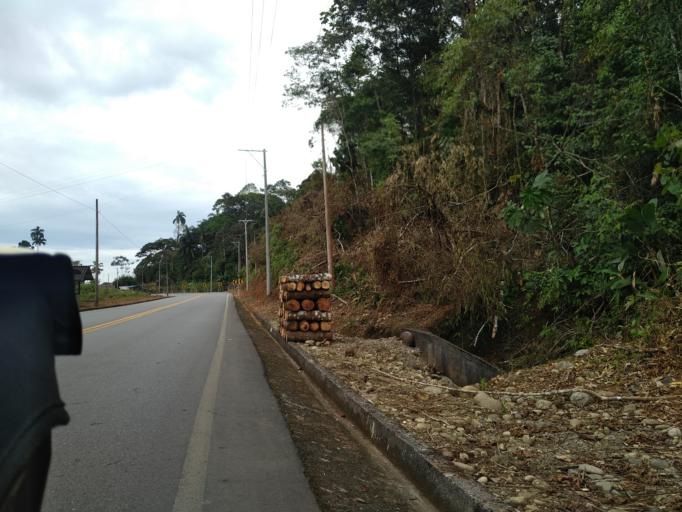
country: EC
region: Pastaza
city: Puyo
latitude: -1.3117
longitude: -77.8871
